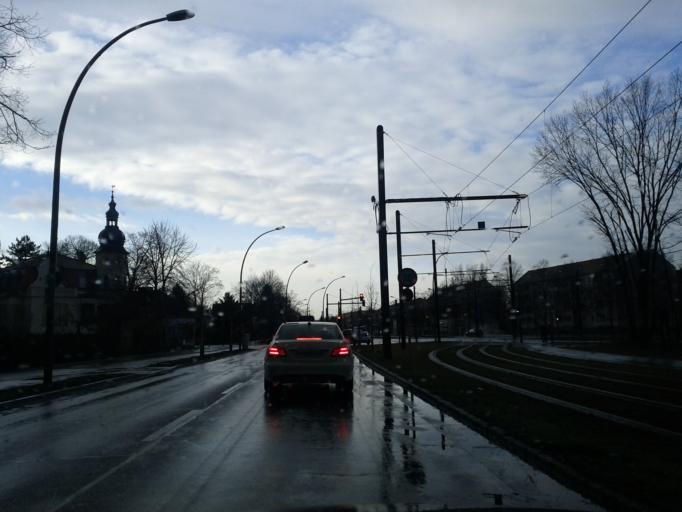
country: DE
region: Berlin
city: Berlin Koepenick
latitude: 52.4512
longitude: 13.6021
